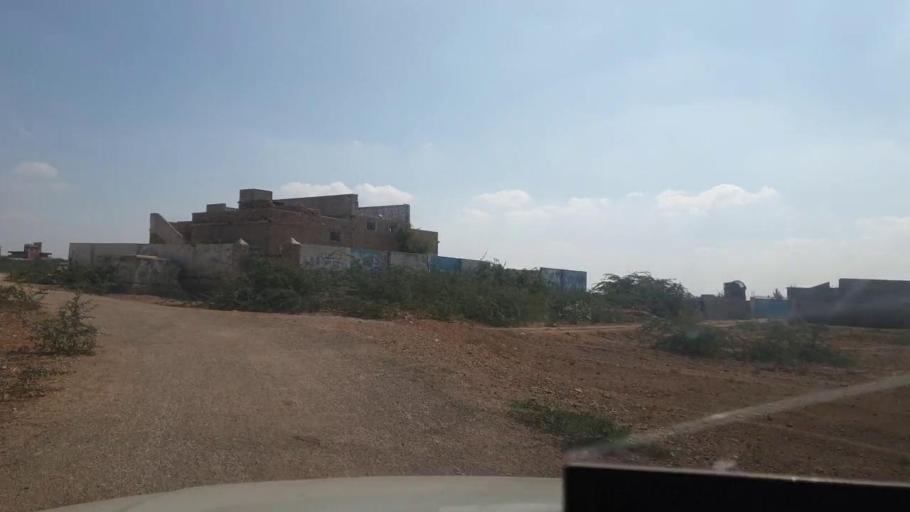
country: PK
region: Sindh
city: Thatta
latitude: 24.8347
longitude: 68.0006
